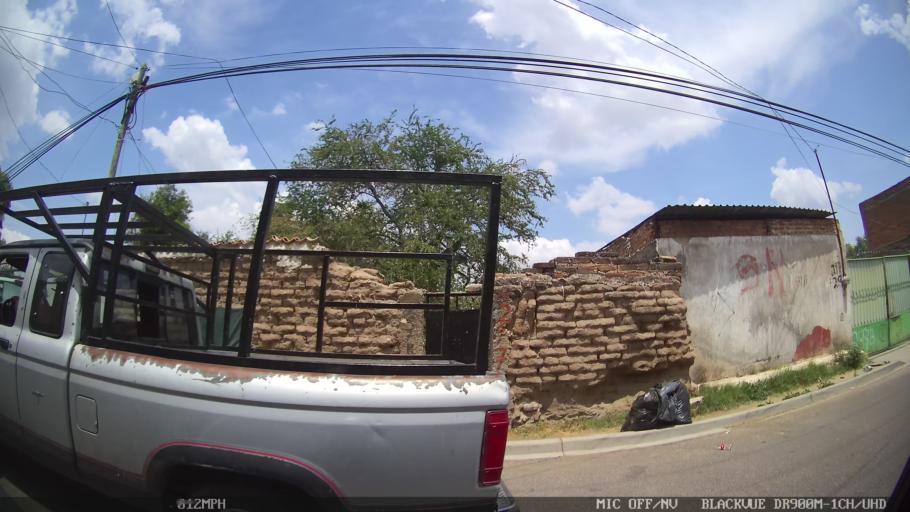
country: MX
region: Jalisco
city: Tonala
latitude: 20.6807
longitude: -103.2454
